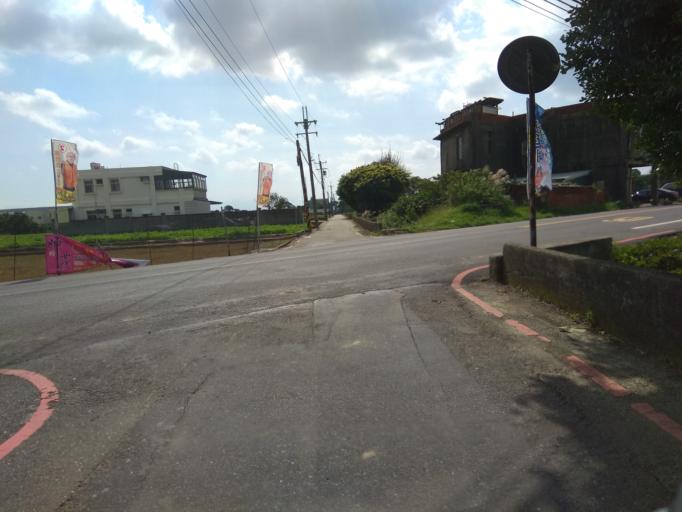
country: TW
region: Taiwan
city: Taoyuan City
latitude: 25.0728
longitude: 121.2490
